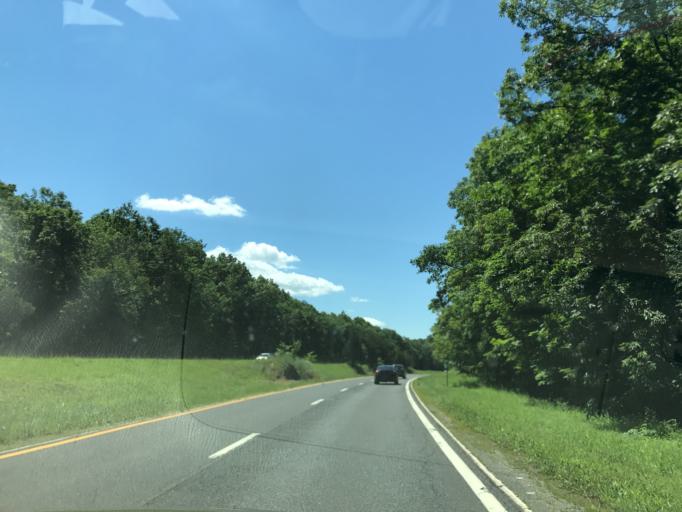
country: US
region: New York
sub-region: Dutchess County
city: Pleasant Valley
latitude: 41.7129
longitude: -73.7827
